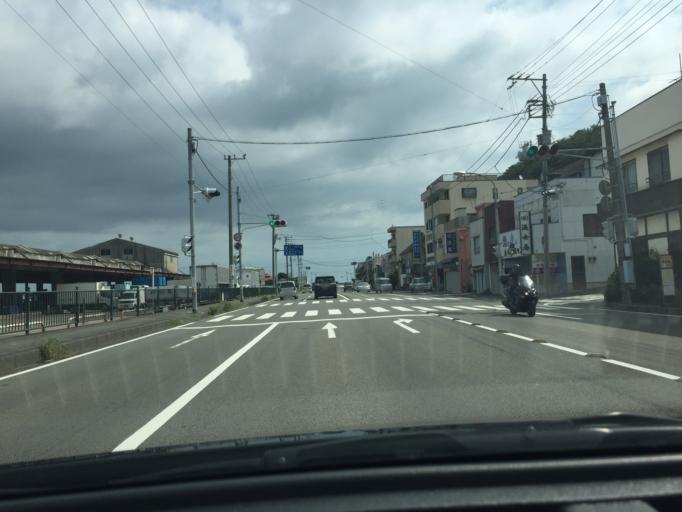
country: JP
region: Shizuoka
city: Ito
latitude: 34.9702
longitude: 139.1074
